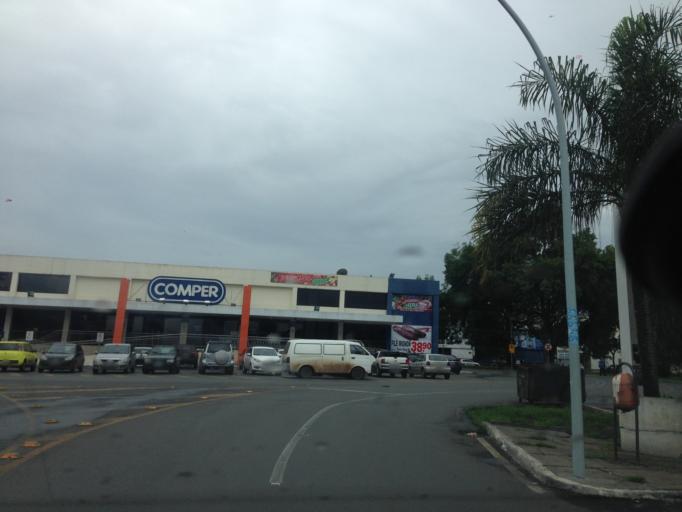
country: BR
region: Federal District
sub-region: Brasilia
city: Brasilia
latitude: -15.8112
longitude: -47.9021
